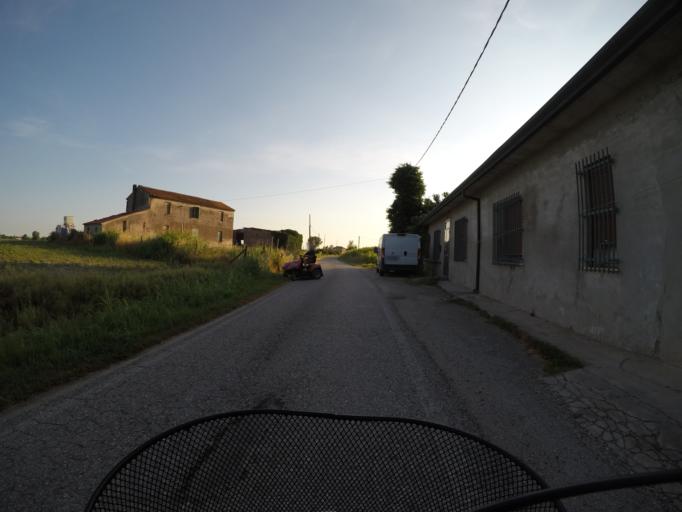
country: IT
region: Veneto
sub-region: Provincia di Rovigo
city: San Bellino
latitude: 45.0184
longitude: 11.6091
